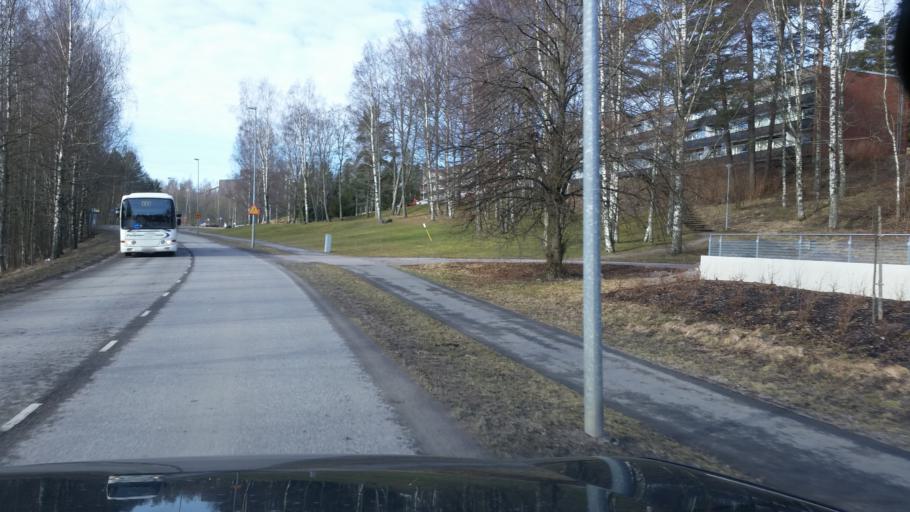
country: FI
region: Uusimaa
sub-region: Helsinki
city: Kirkkonummi
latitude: 60.0915
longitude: 24.3900
